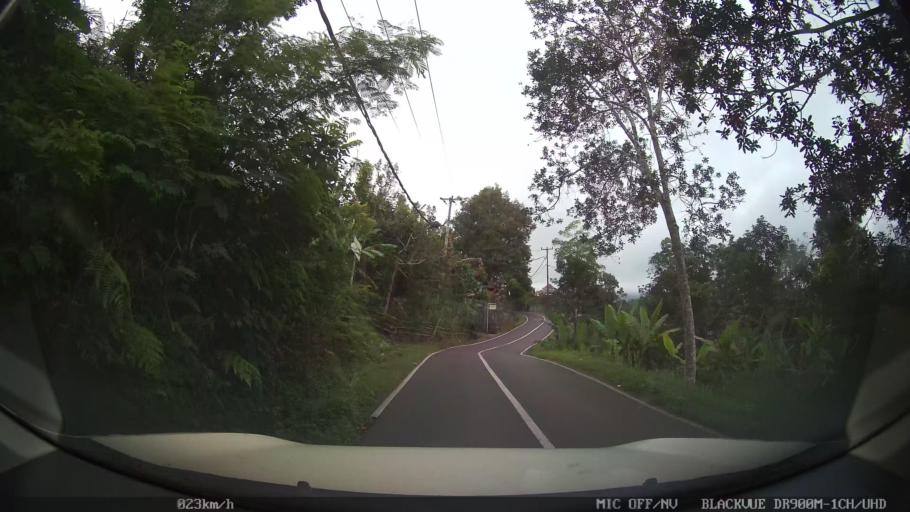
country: ID
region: Bali
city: Banjar Geriana Kangin
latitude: -8.3831
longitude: 115.4447
